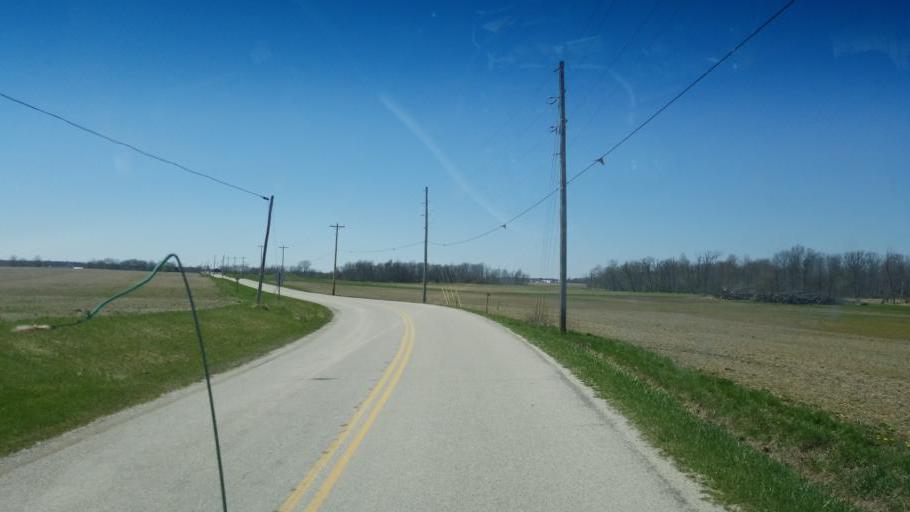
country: US
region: Ohio
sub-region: Huron County
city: Willard
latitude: 41.0528
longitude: -82.8951
